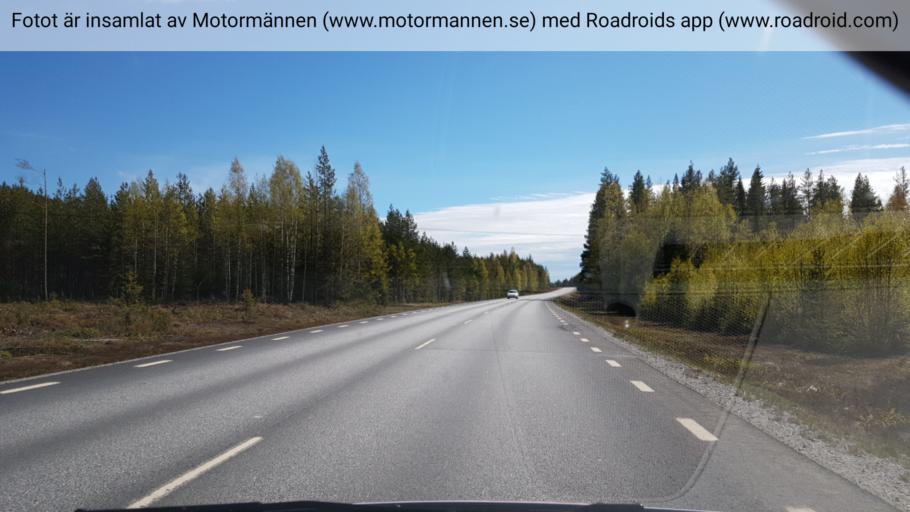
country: SE
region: Vaesterbotten
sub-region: Vannas Kommun
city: Vannasby
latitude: 64.0703
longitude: 19.9914
